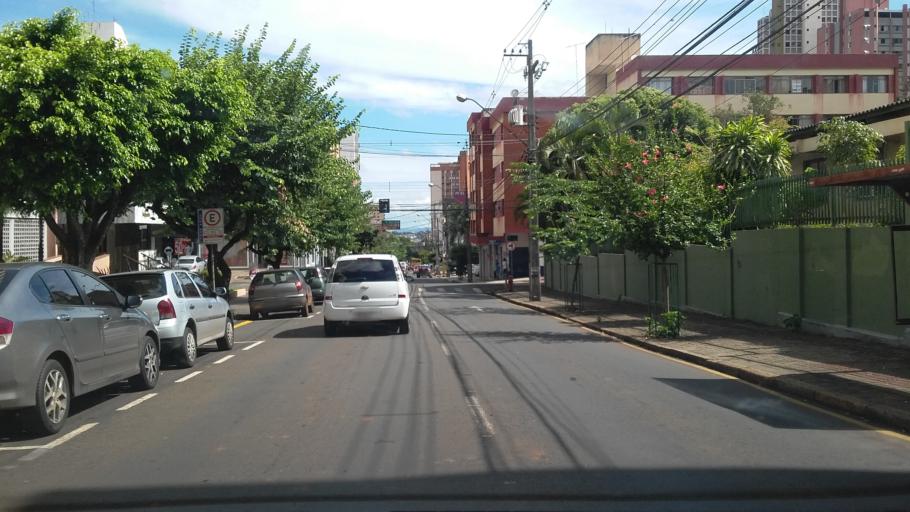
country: BR
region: Parana
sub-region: Londrina
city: Londrina
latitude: -23.3128
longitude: -51.1628
